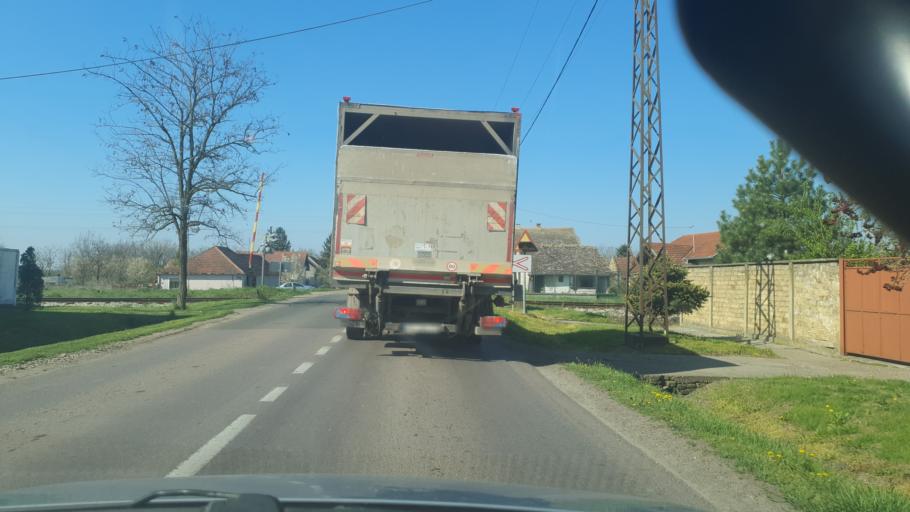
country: RS
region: Autonomna Pokrajina Vojvodina
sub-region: Zapadnobacki Okrug
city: Sombor
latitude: 45.7691
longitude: 19.2670
